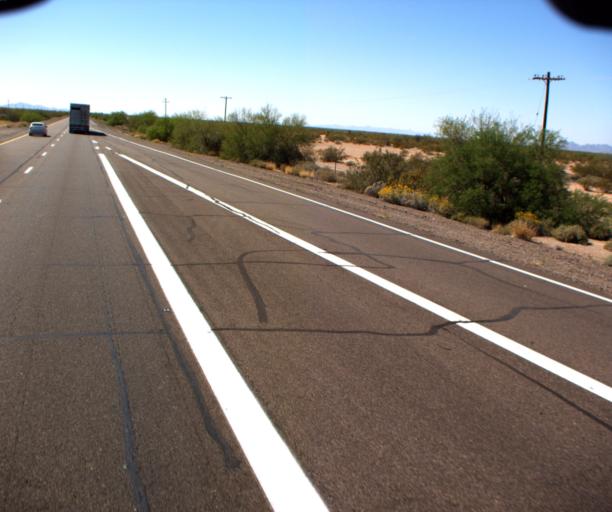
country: US
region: Arizona
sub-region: Maricopa County
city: Gila Bend
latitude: 32.8352
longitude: -113.3620
